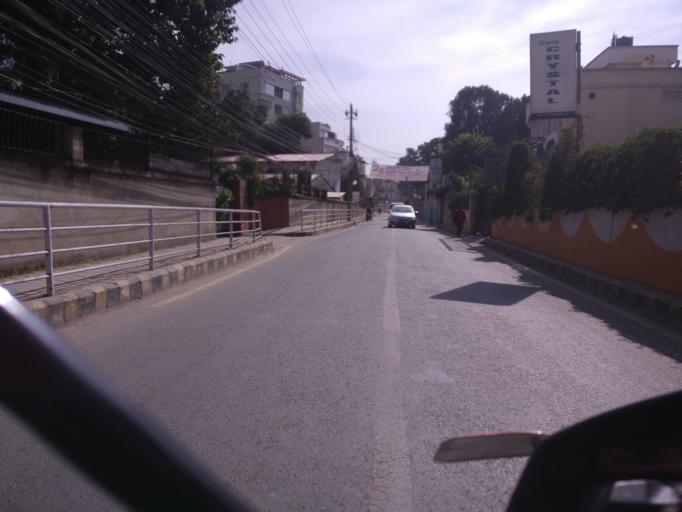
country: NP
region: Central Region
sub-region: Bagmati Zone
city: Patan
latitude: 27.6707
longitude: 85.3161
